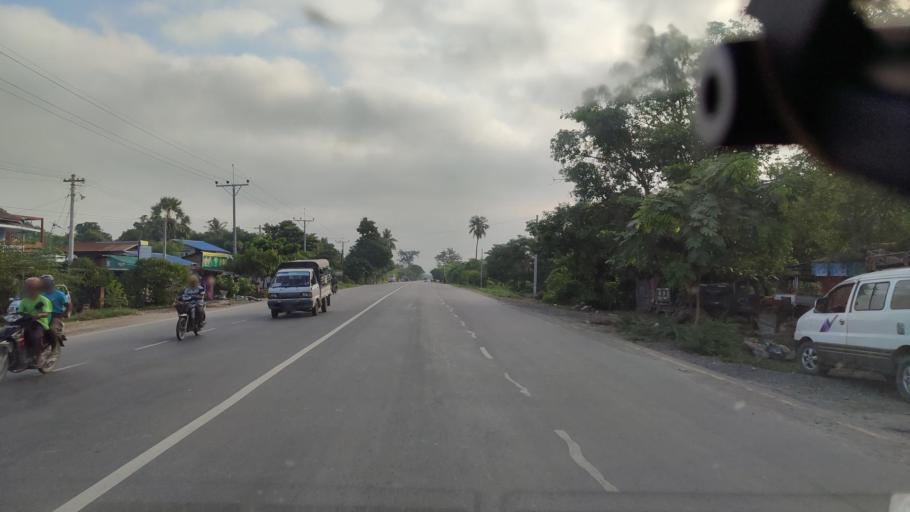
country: MM
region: Mandalay
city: Mandalay
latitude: 22.0683
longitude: 96.1333
